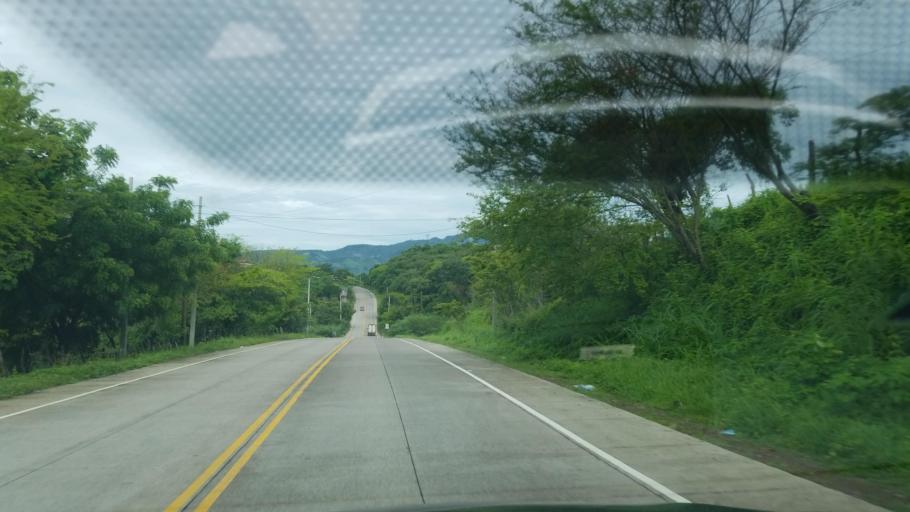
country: HN
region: Choluteca
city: Pespire
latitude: 13.6709
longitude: -87.3548
